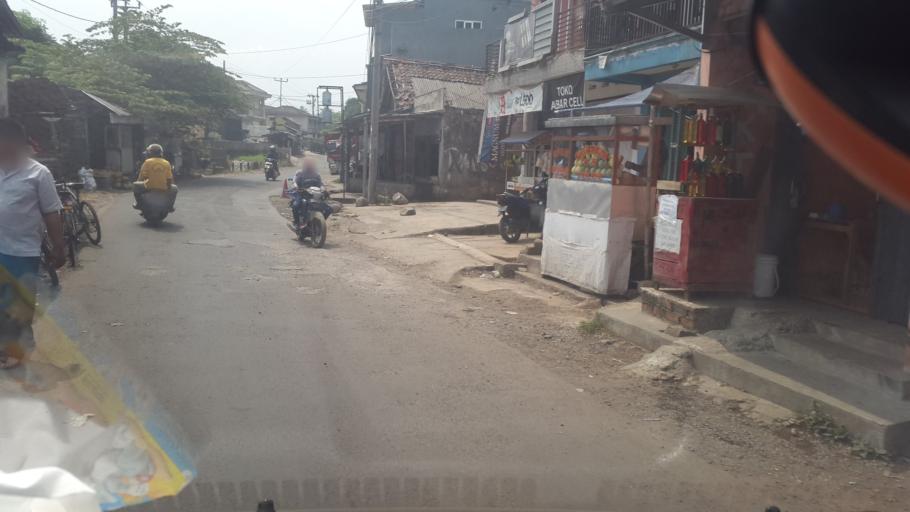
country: ID
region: West Java
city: Sukabumi
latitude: -6.9012
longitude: 106.8818
